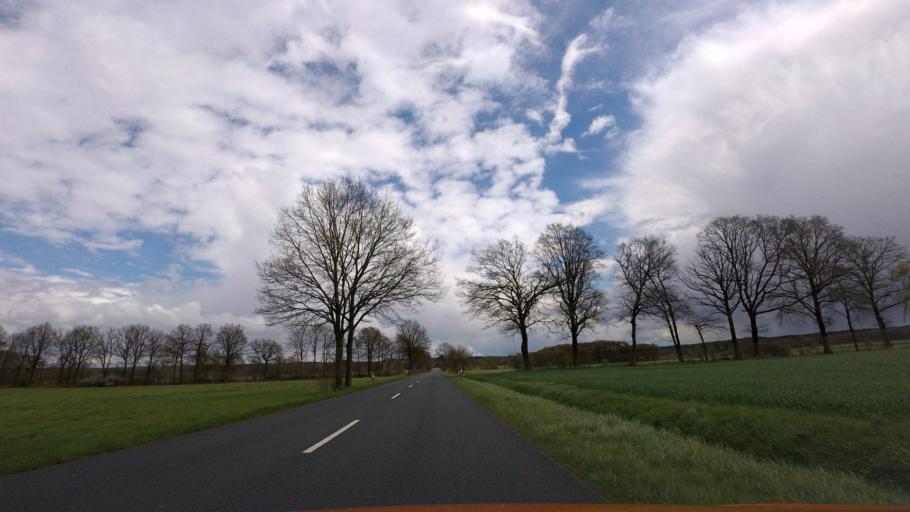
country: DE
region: Lower Saxony
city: Oldendorf
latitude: 53.1755
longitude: 10.1970
